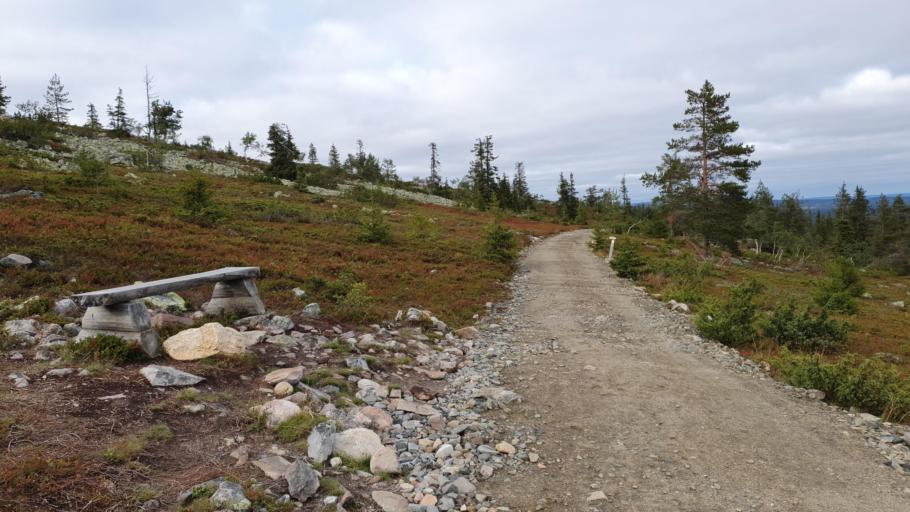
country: FI
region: Lapland
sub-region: Tunturi-Lappi
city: Kolari
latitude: 67.5635
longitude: 24.2552
